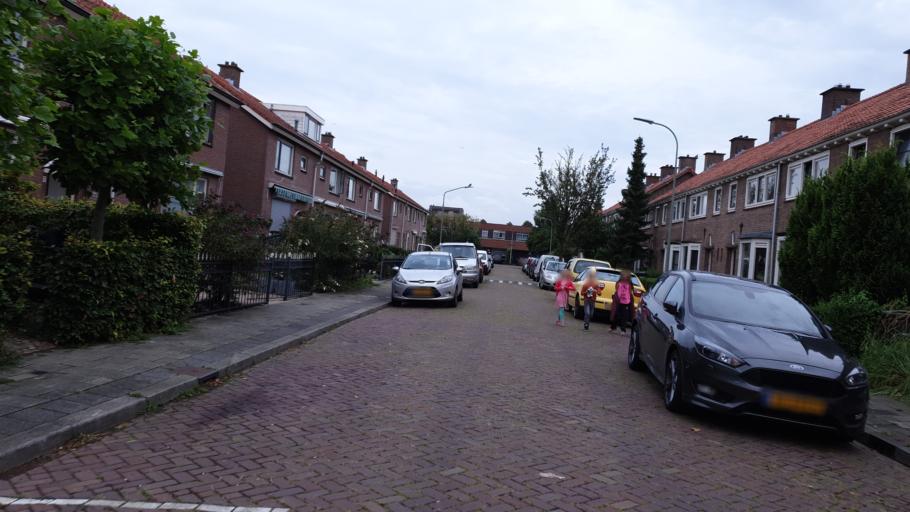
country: NL
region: South Holland
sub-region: Gemeente Dordrecht
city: Dordrecht
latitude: 51.8027
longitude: 4.6675
